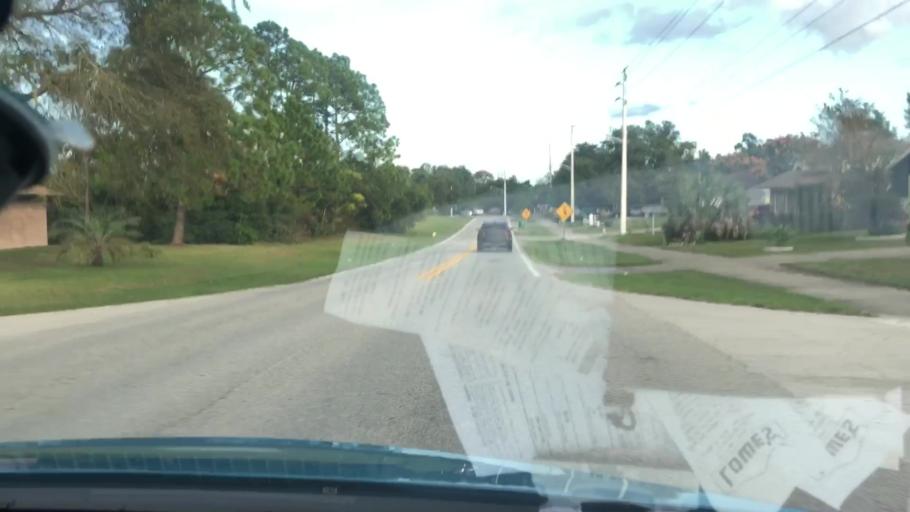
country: US
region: Florida
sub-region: Volusia County
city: Deltona
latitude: 28.9206
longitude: -81.2005
